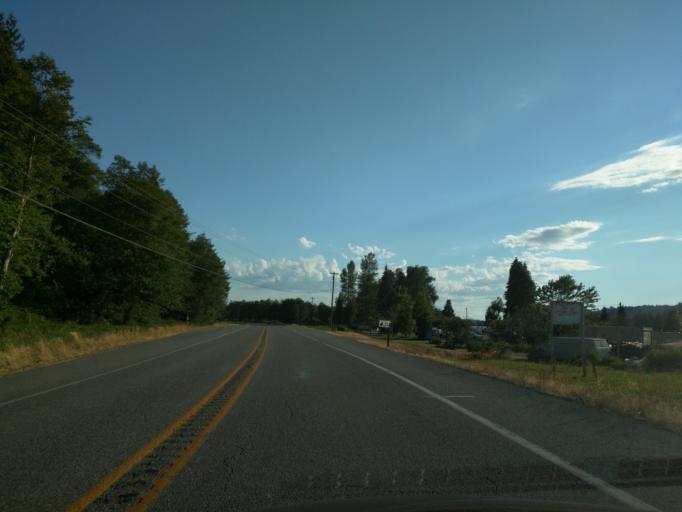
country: US
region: Washington
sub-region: Snohomish County
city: Arlington Heights
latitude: 48.2647
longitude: -122.0204
